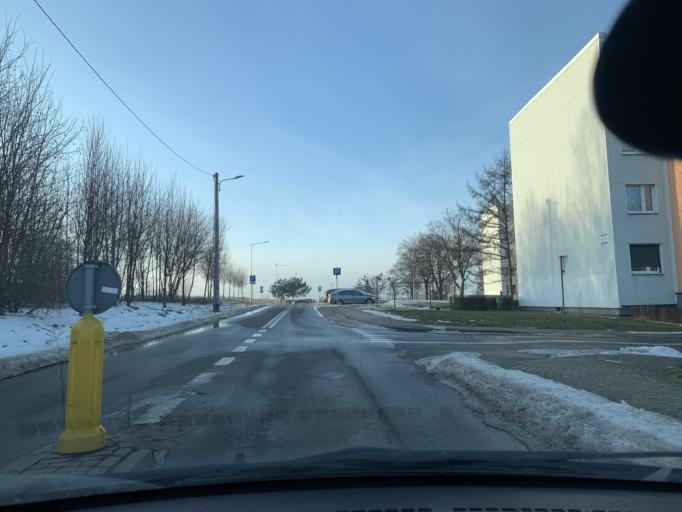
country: PL
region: Silesian Voivodeship
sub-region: Powiat tarnogorski
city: Radzionkow
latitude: 50.4047
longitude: 18.8956
